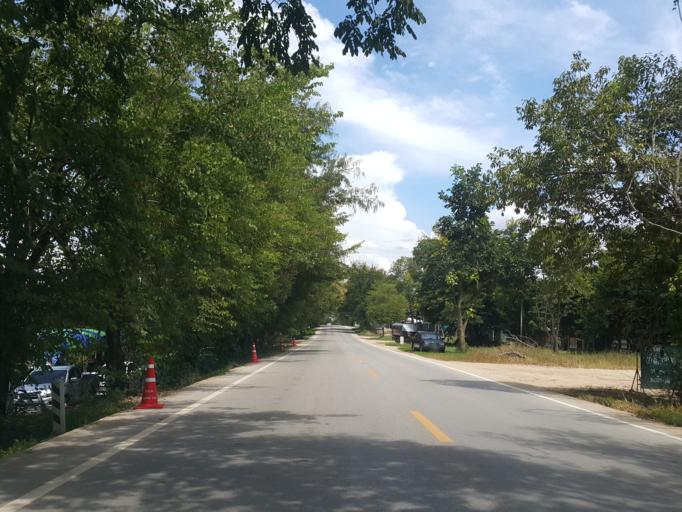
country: TH
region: Chiang Mai
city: Phrao
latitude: 19.2979
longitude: 99.1888
